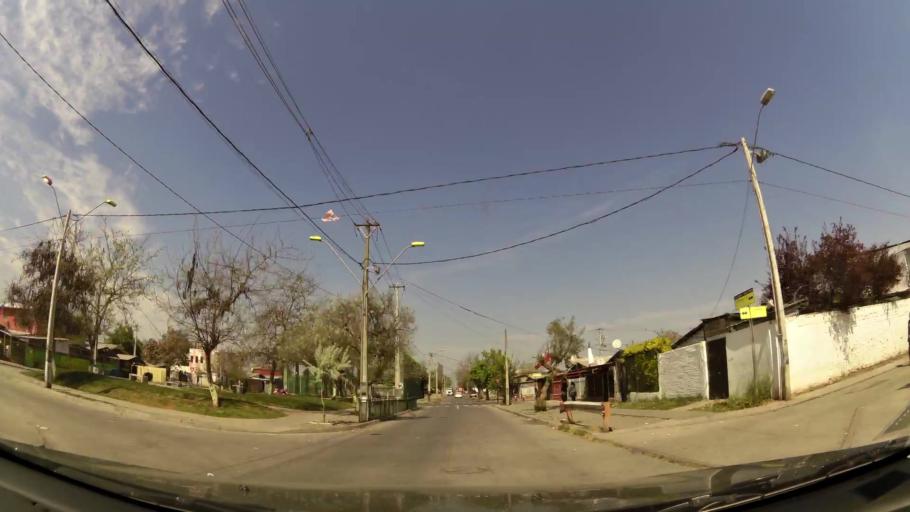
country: CL
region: Santiago Metropolitan
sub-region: Provincia de Santiago
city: La Pintana
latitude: -33.5899
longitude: -70.6129
